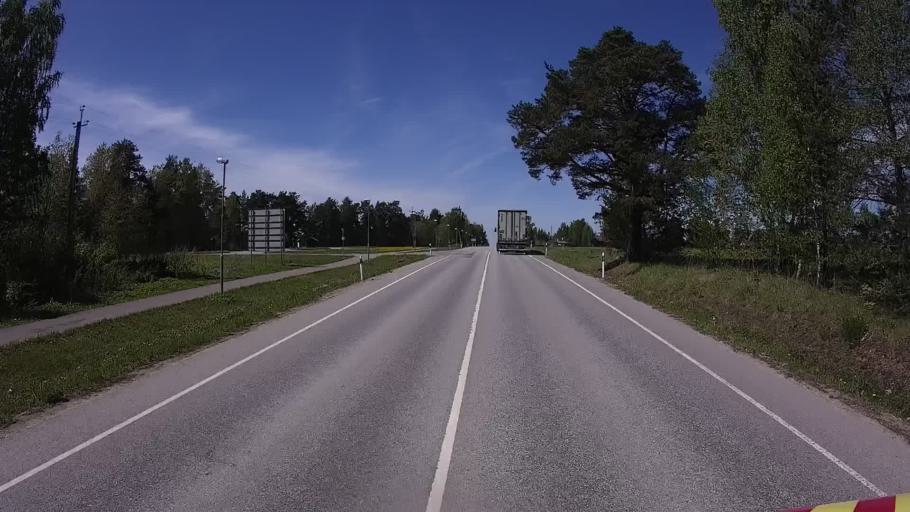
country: EE
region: Vorumaa
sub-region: Voru linn
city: Voru
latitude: 57.8108
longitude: 27.0587
